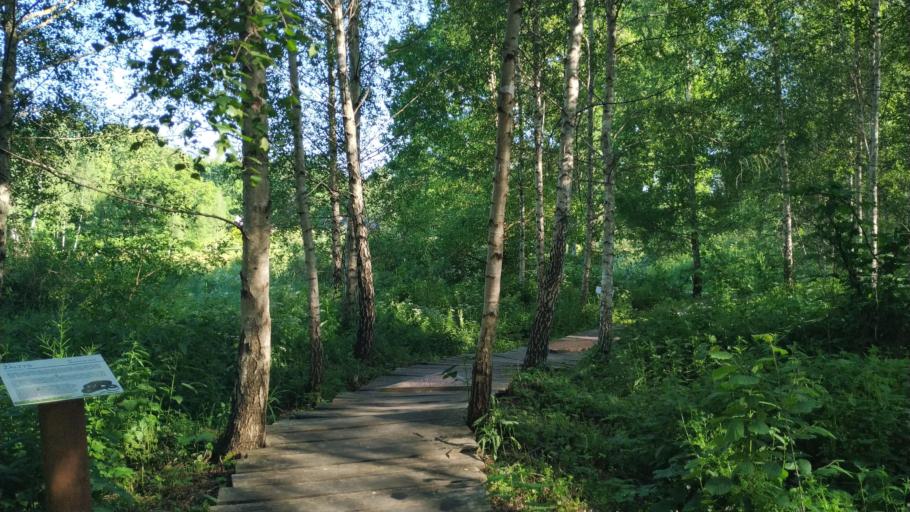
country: LT
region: Utenos apskritis
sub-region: Anyksciai
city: Anyksciai
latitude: 55.4762
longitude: 25.0542
